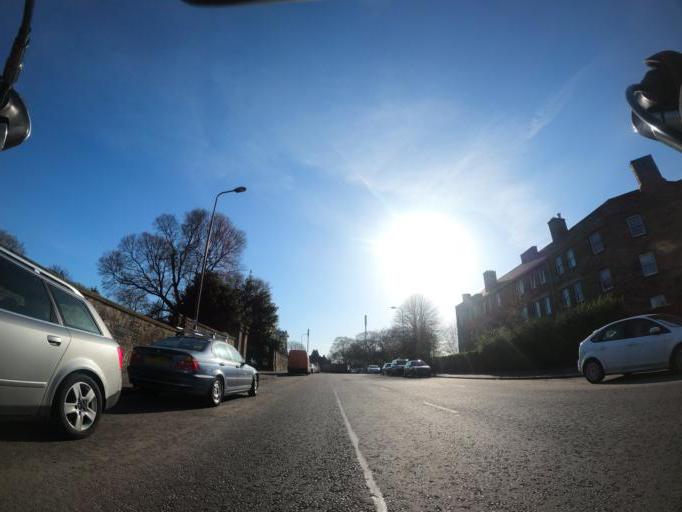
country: GB
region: Scotland
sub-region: Edinburgh
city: Edinburgh
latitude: 55.9683
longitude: -3.1859
